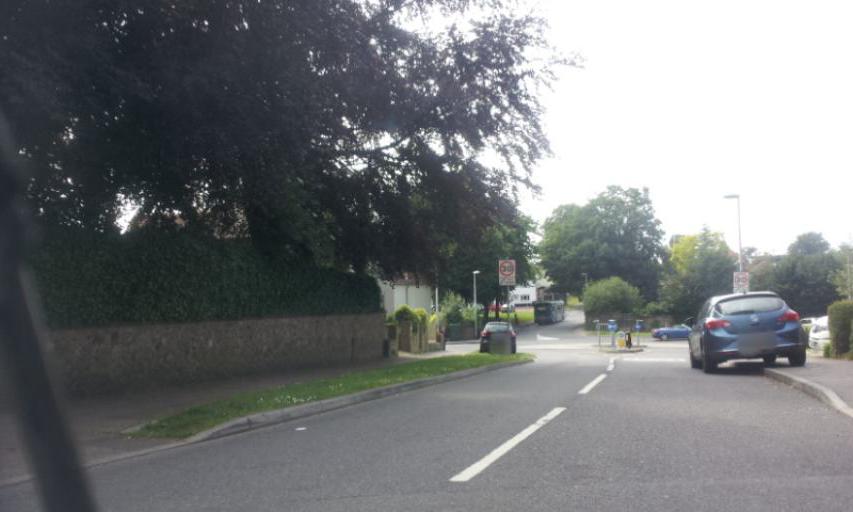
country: GB
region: England
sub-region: Kent
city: Gillingham
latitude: 51.3879
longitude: 0.5750
